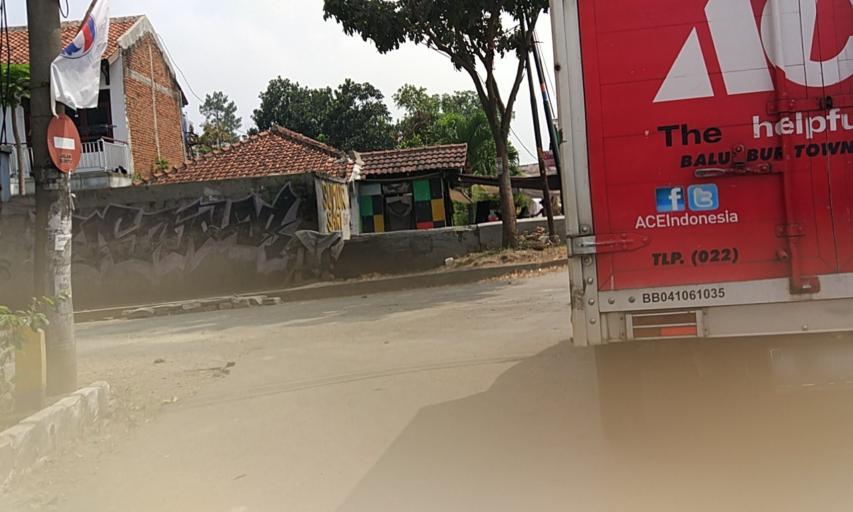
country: ID
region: West Java
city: Margahayukencana
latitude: -6.9473
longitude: 107.5614
